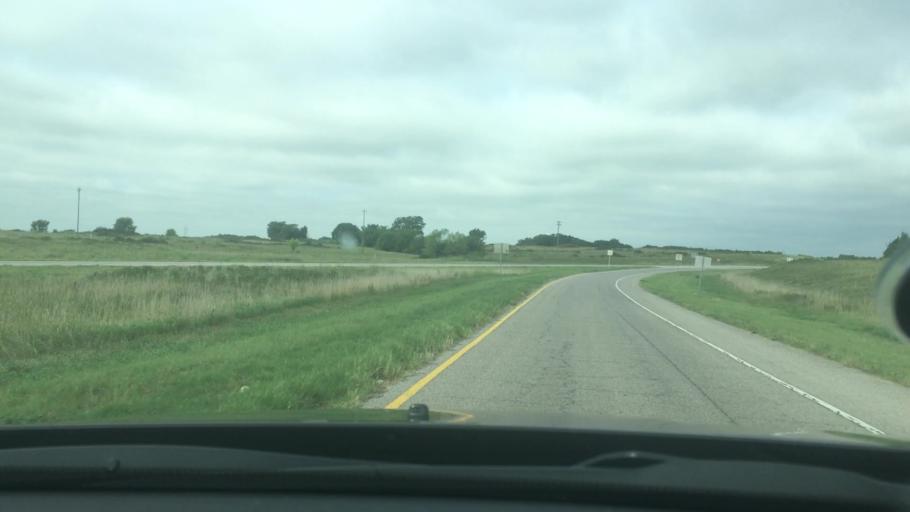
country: US
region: Oklahoma
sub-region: Pontotoc County
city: Ada
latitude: 34.6429
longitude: -96.5322
